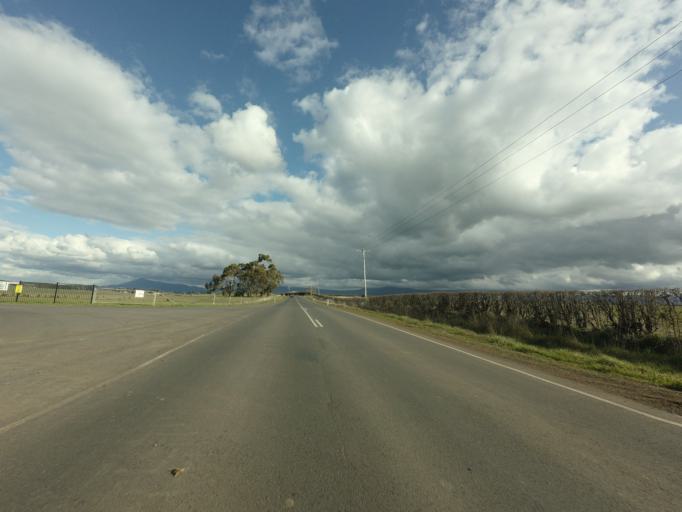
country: AU
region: Tasmania
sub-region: Northern Midlands
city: Longford
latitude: -41.7005
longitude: 147.0772
